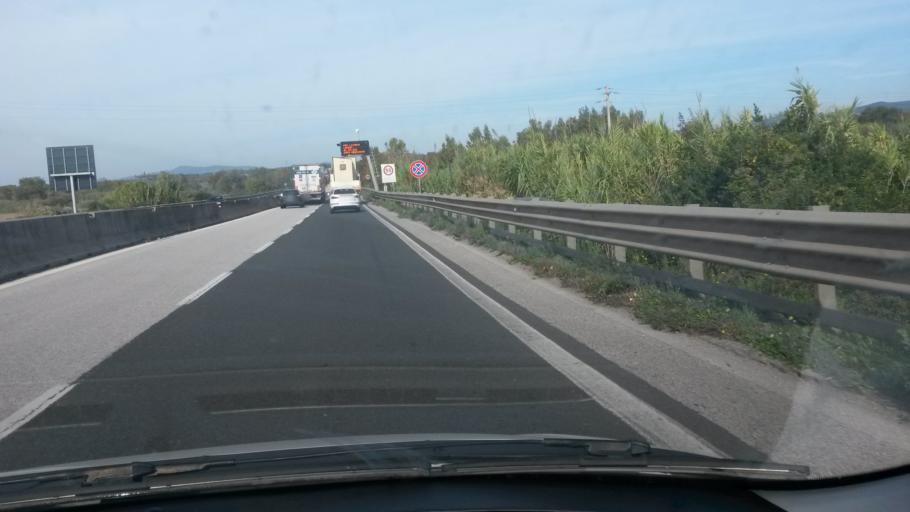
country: IT
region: Tuscany
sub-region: Provincia di Livorno
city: Cecina
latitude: 43.3204
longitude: 10.5326
